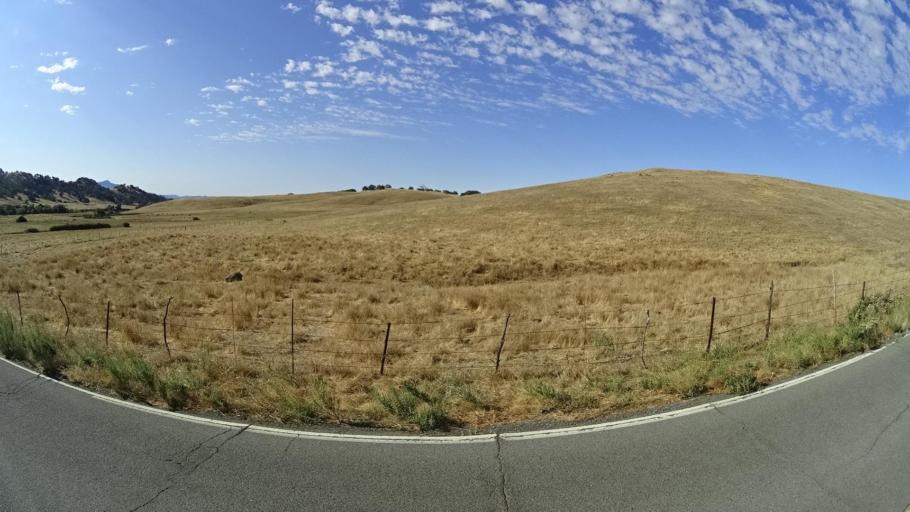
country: US
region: California
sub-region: San Diego County
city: Julian
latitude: 33.1635
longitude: -116.7323
